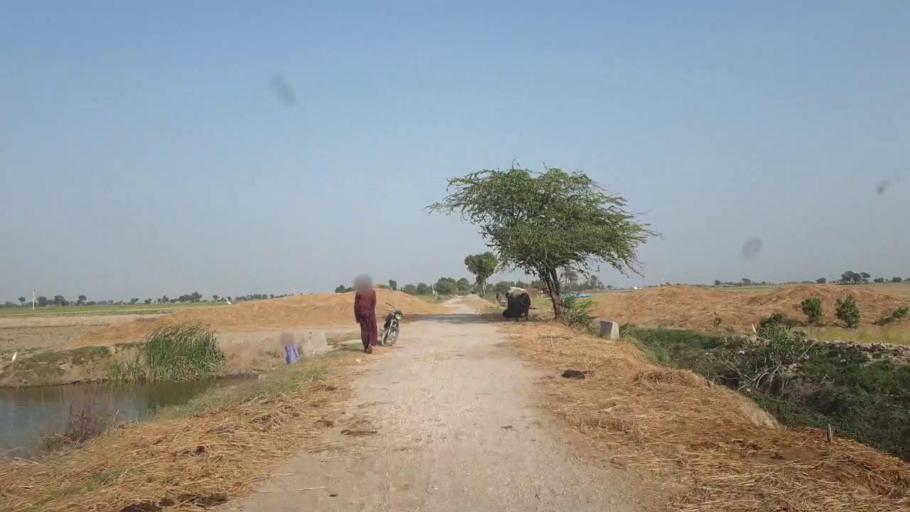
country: PK
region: Sindh
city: Kario
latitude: 24.5998
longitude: 68.5416
